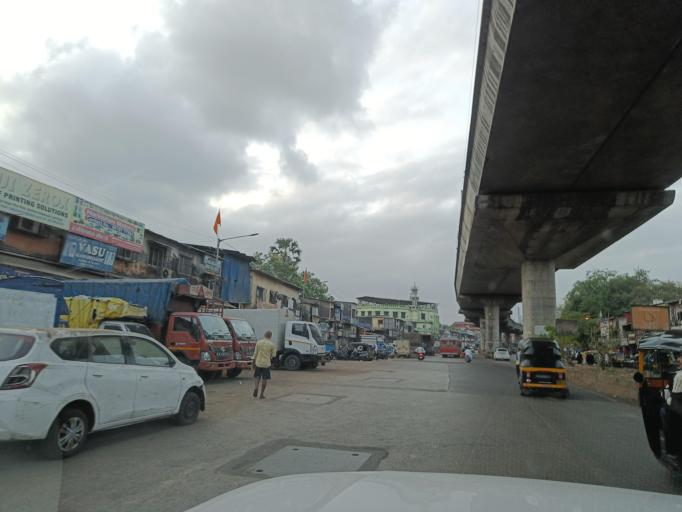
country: IN
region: Maharashtra
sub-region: Mumbai Suburban
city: Powai
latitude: 19.1023
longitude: 72.8898
